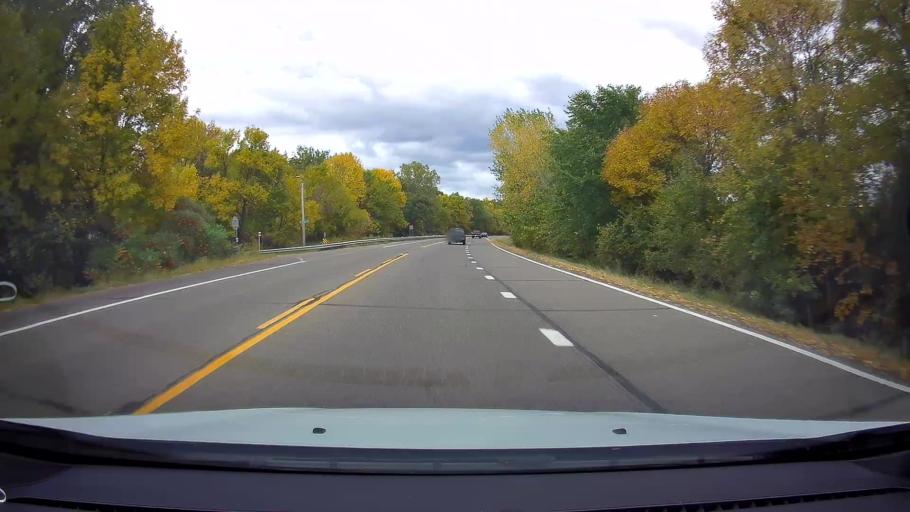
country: US
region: Minnesota
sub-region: Chisago County
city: Chisago City
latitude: 45.3442
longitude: -92.9120
